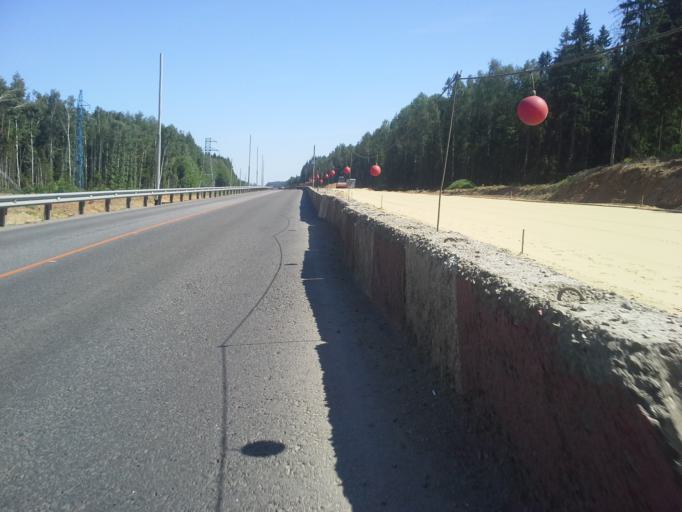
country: RU
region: Moskovskaya
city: Aprelevka
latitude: 55.4684
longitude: 37.0828
